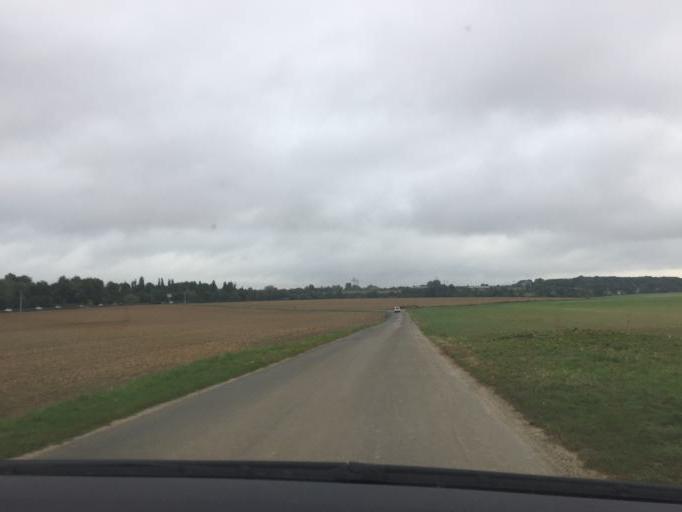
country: FR
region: Ile-de-France
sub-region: Departement de l'Essonne
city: Saclay
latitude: 48.7342
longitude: 2.1758
